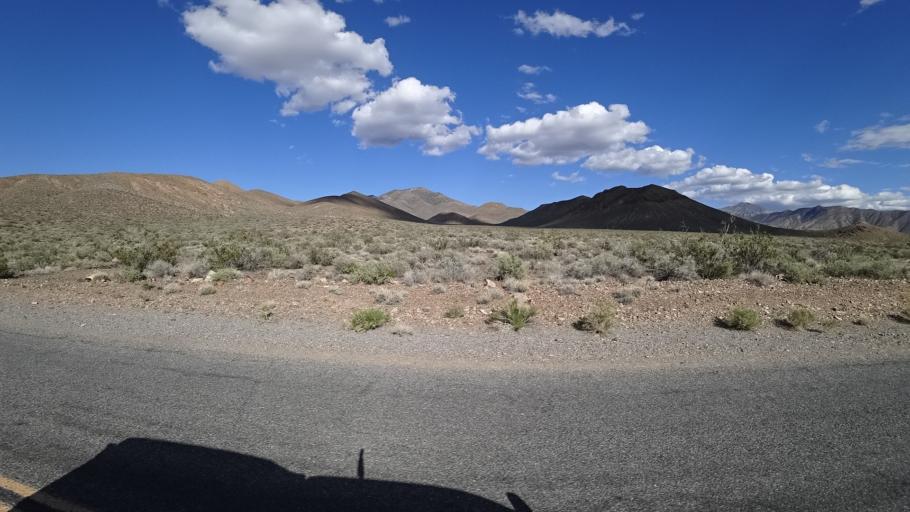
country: US
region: California
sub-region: San Bernardino County
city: Searles Valley
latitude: 36.2926
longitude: -117.1755
